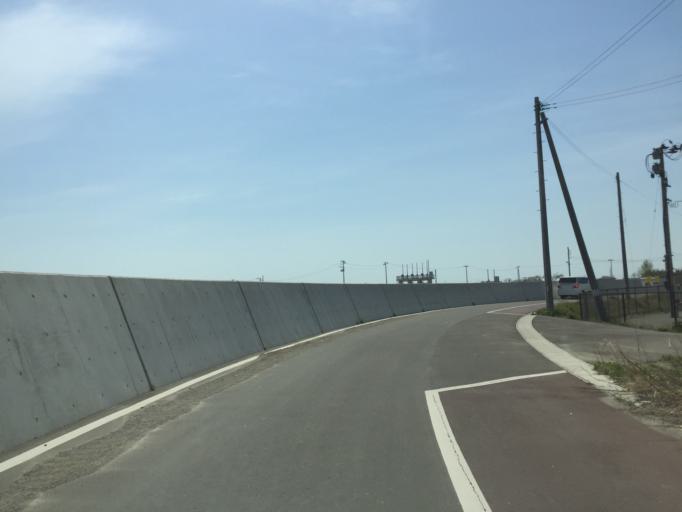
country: JP
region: Miyagi
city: Watari
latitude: 38.0330
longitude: 140.8976
